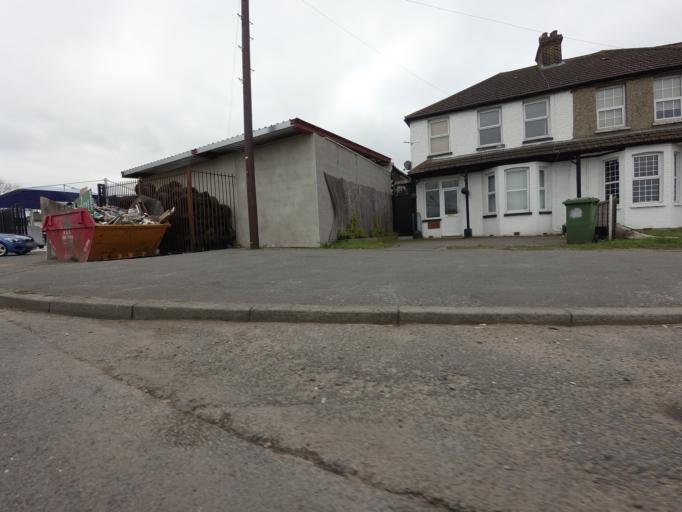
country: GB
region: England
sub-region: Greater London
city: Bexley
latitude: 51.4106
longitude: 0.1425
